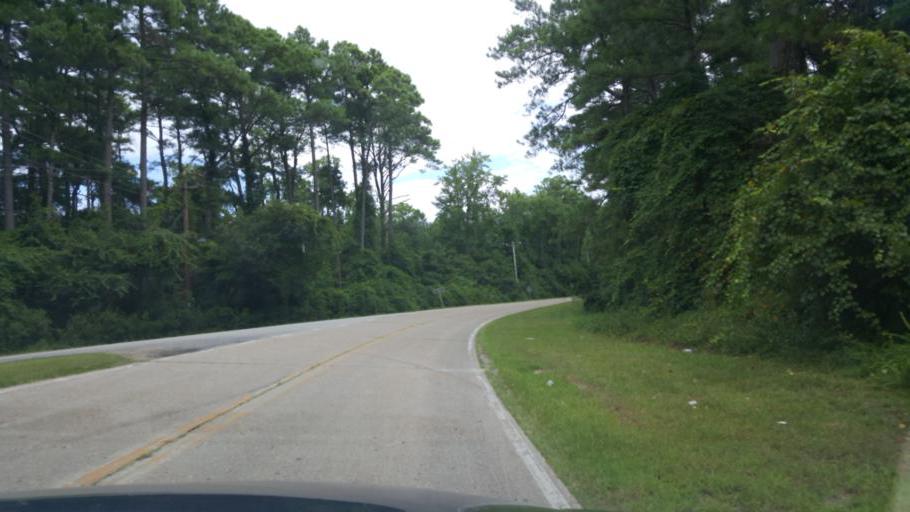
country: US
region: North Carolina
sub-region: Dare County
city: Manteo
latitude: 35.9216
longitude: -75.7061
